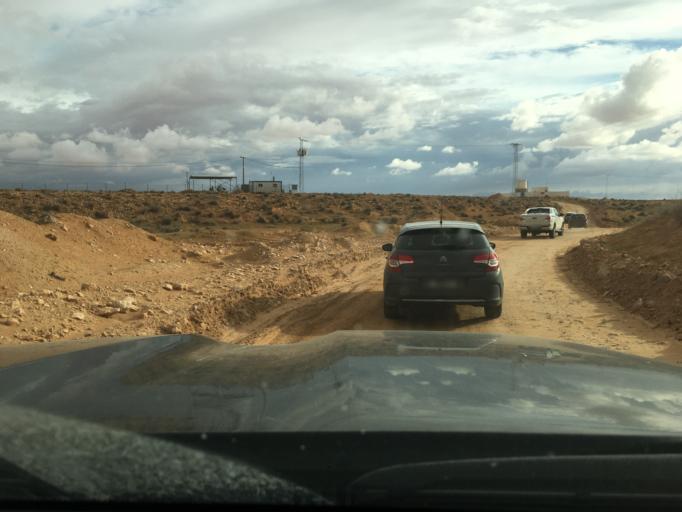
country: TN
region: Madanin
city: Medenine
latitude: 33.2683
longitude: 10.5694
